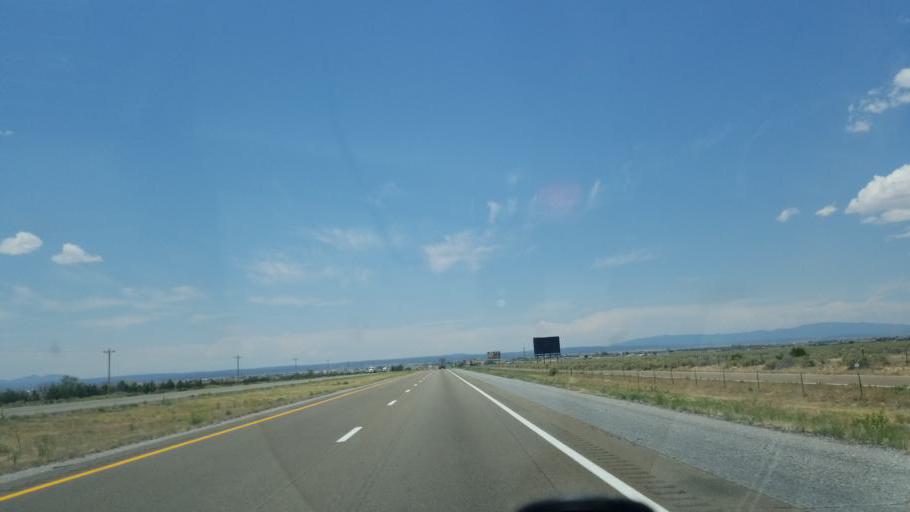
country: US
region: New Mexico
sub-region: Torrance County
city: Moriarty
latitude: 35.0049
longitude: -105.9830
